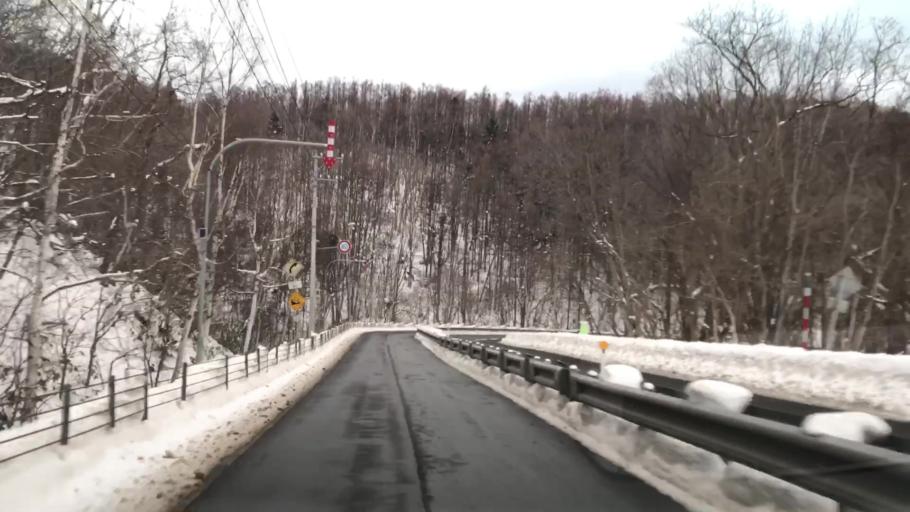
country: JP
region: Hokkaido
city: Yoichi
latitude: 43.2913
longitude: 140.5856
